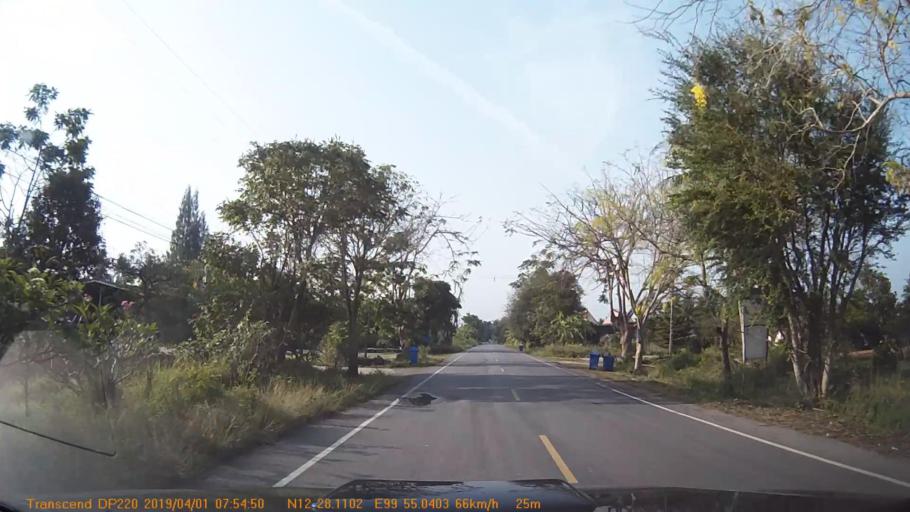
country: TH
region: Prachuap Khiri Khan
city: Pran Buri
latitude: 12.4681
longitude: 99.9174
